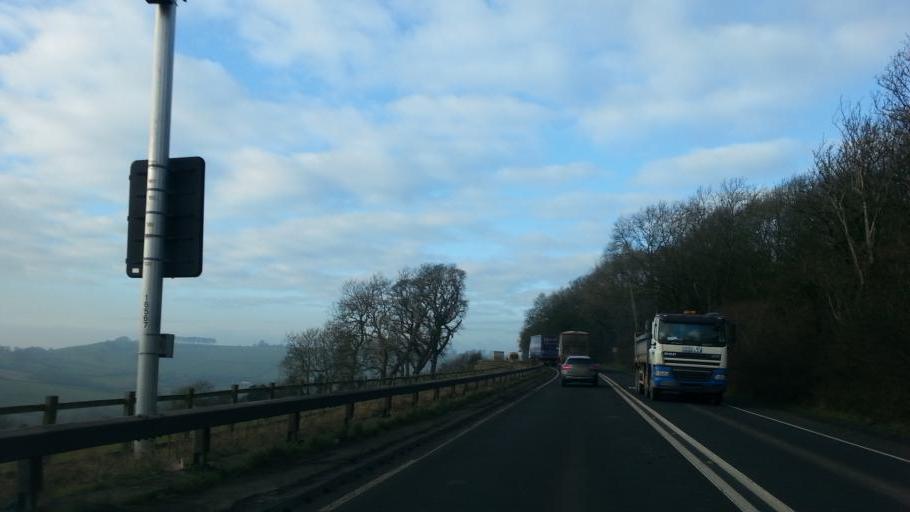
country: GB
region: England
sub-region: South Gloucestershire
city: Cold Ashton
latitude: 51.4313
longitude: -2.3633
